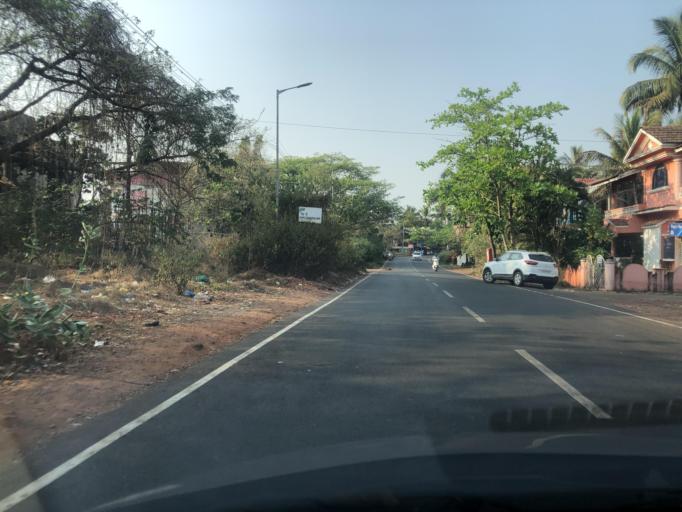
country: IN
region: Goa
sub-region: North Goa
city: Serula
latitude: 15.5283
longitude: 73.8292
